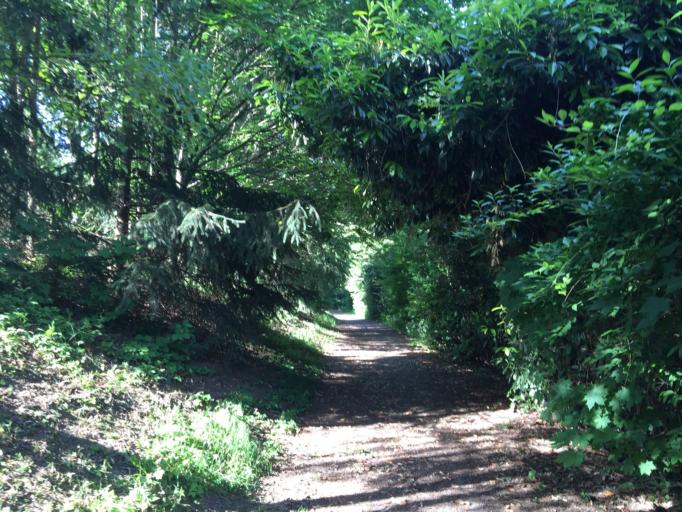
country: FR
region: Rhone-Alpes
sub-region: Departement de la Loire
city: Saint-Priest-en-Jarez
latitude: 45.4625
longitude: 4.3728
